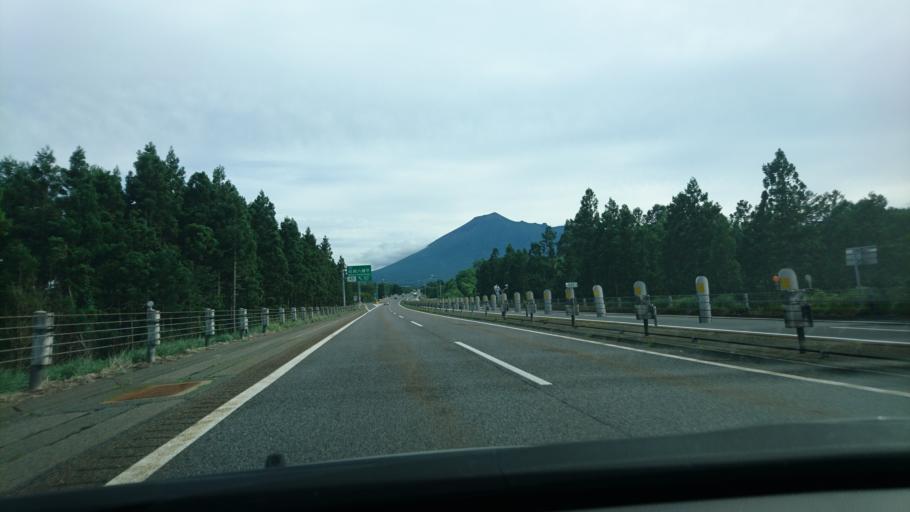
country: JP
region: Iwate
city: Shizukuishi
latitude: 39.9539
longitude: 141.0325
